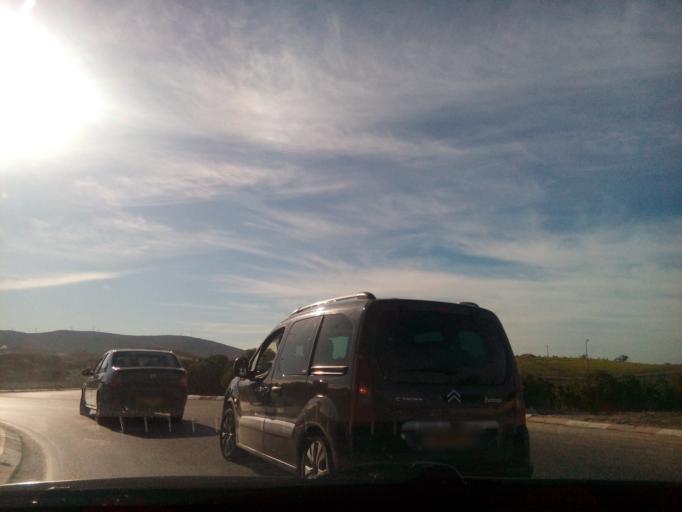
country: DZ
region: Tlemcen
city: Hennaya
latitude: 34.9259
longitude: -1.3597
